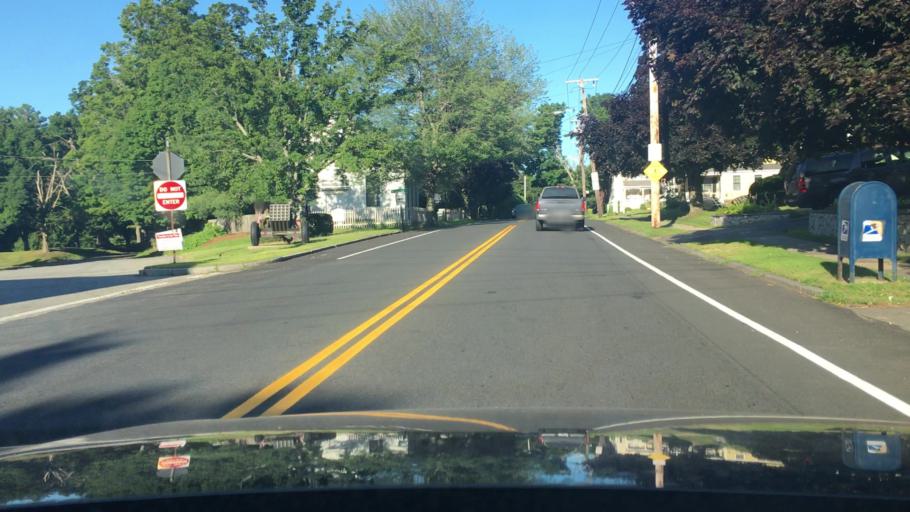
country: US
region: Massachusetts
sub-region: Essex County
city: Amesbury
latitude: 42.8551
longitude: -70.9378
